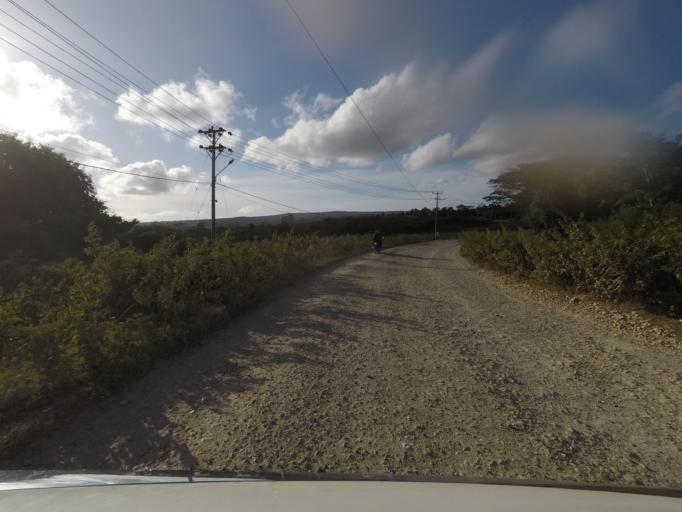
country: TL
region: Lautem
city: Lospalos
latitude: -8.4550
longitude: 127.0005
